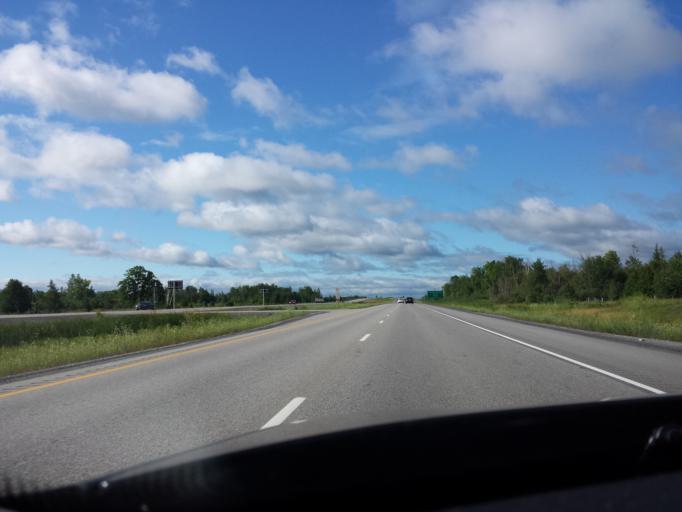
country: CA
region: Ontario
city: Carleton Place
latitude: 45.1871
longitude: -76.0460
